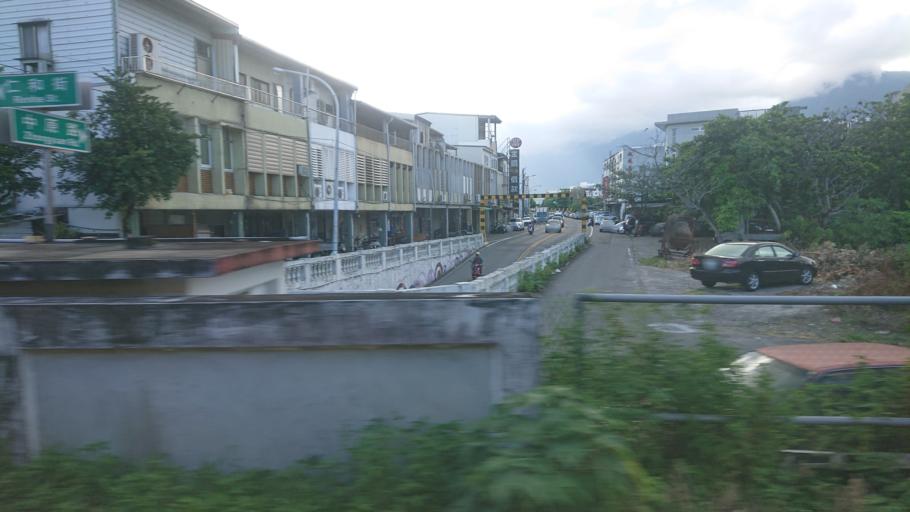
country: TW
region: Taiwan
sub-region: Hualien
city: Hualian
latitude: 23.9764
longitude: 121.5928
